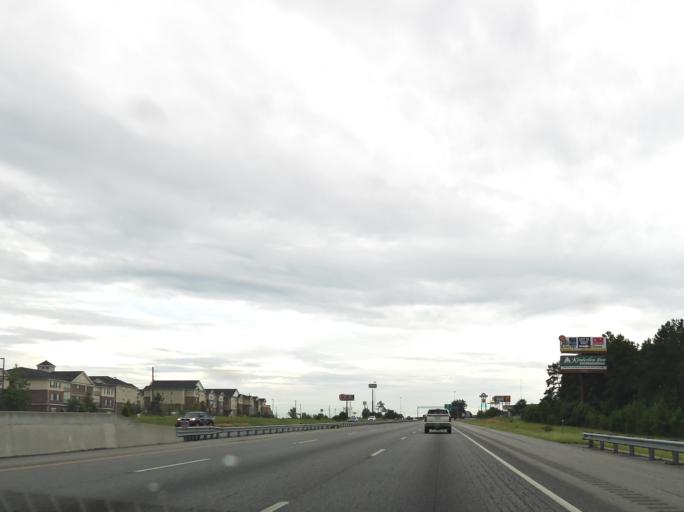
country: US
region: Georgia
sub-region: Lowndes County
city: Remerton
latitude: 30.8515
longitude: -83.3332
